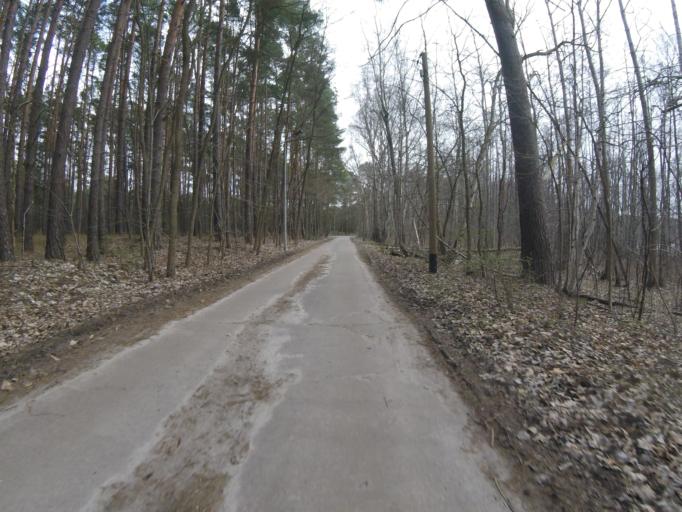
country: DE
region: Brandenburg
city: Gross Koris
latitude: 52.1783
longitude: 13.6487
